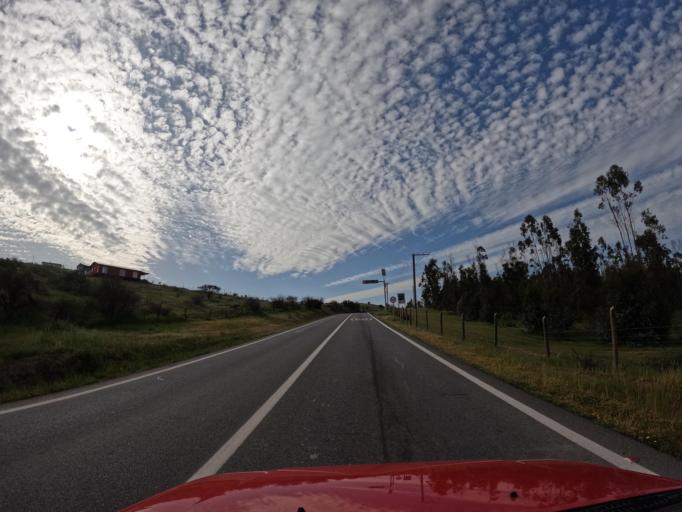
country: CL
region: O'Higgins
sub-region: Provincia de Colchagua
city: Santa Cruz
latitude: -34.2692
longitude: -71.7336
